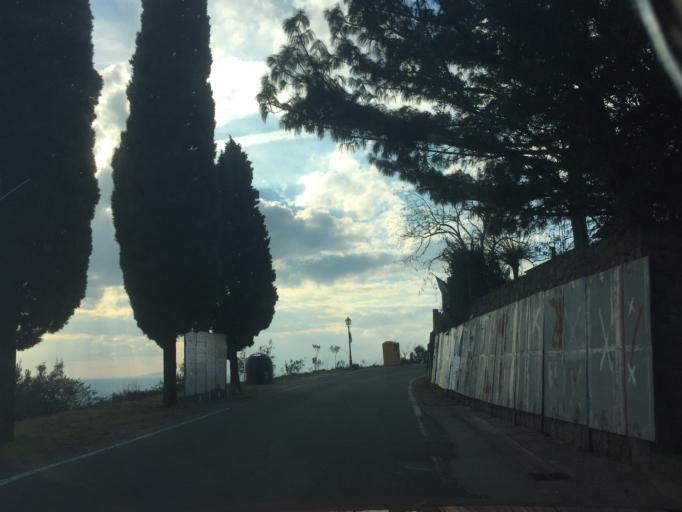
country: IT
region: Tuscany
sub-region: Provincia di Pistoia
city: Larciano
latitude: 43.8216
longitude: 10.9263
